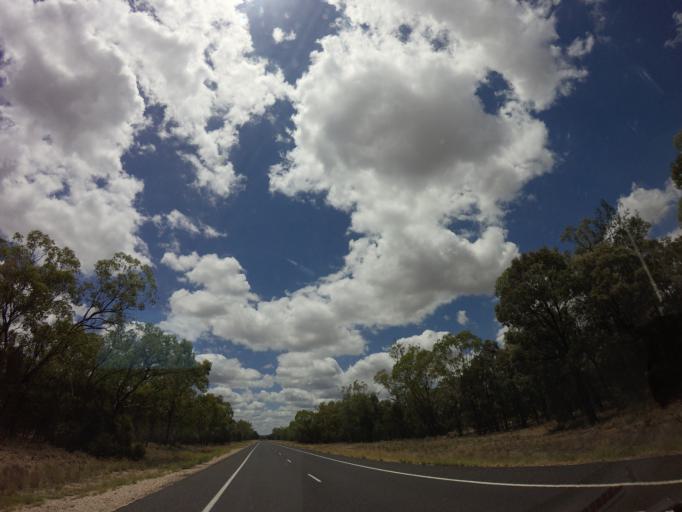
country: AU
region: Queensland
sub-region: Goondiwindi
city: Goondiwindi
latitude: -28.1035
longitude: 150.7229
